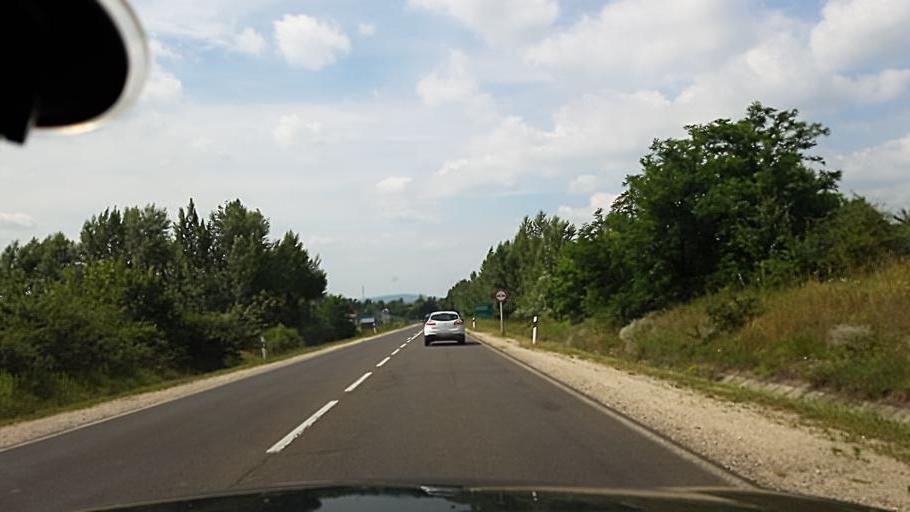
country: HU
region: Komarom-Esztergom
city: Dorog
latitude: 47.7441
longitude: 18.7399
